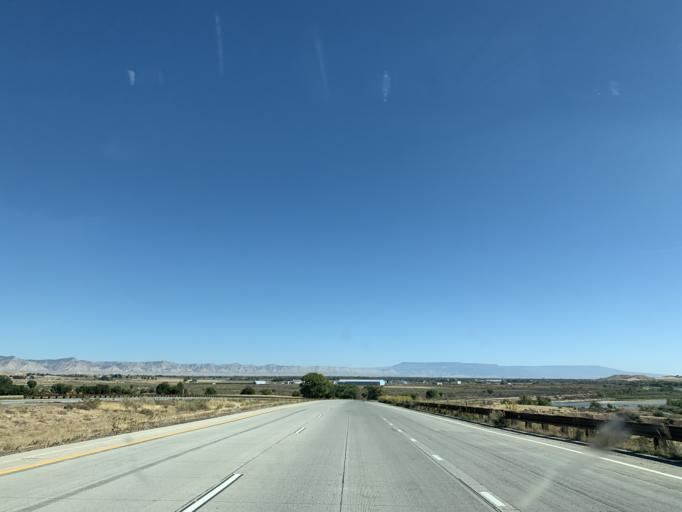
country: US
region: Colorado
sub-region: Mesa County
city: Loma
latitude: 39.1776
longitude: -108.8088
